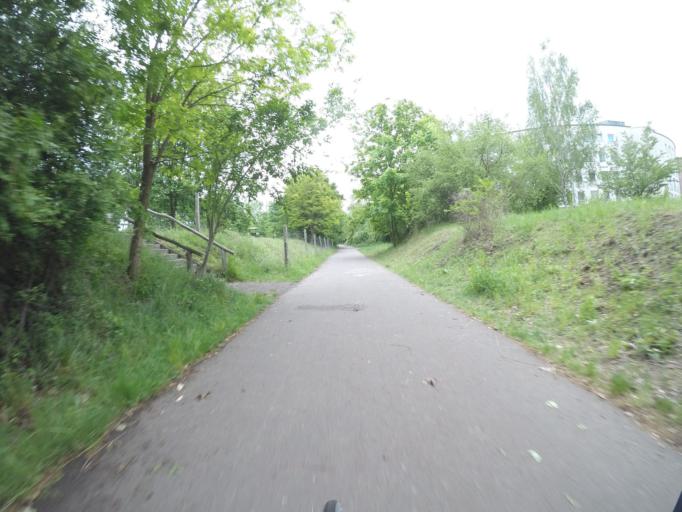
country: DE
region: Berlin
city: Lichtenberg
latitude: 52.5281
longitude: 13.5037
